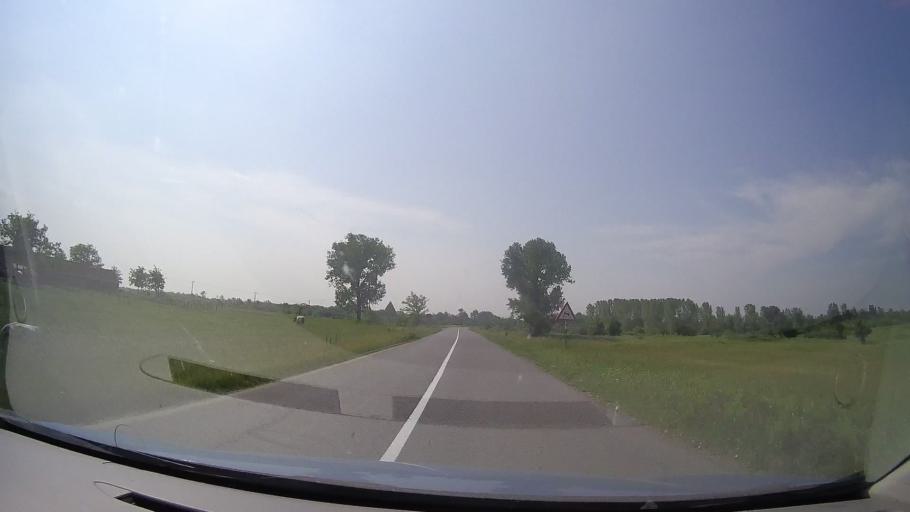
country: RS
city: Jarkovac
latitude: 45.2773
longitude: 20.7632
